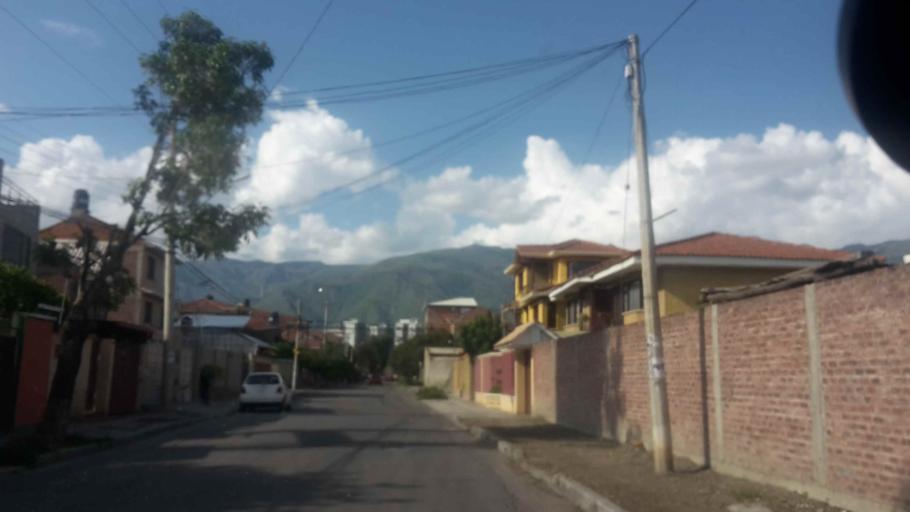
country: BO
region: Cochabamba
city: Cochabamba
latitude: -17.3799
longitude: -66.1944
